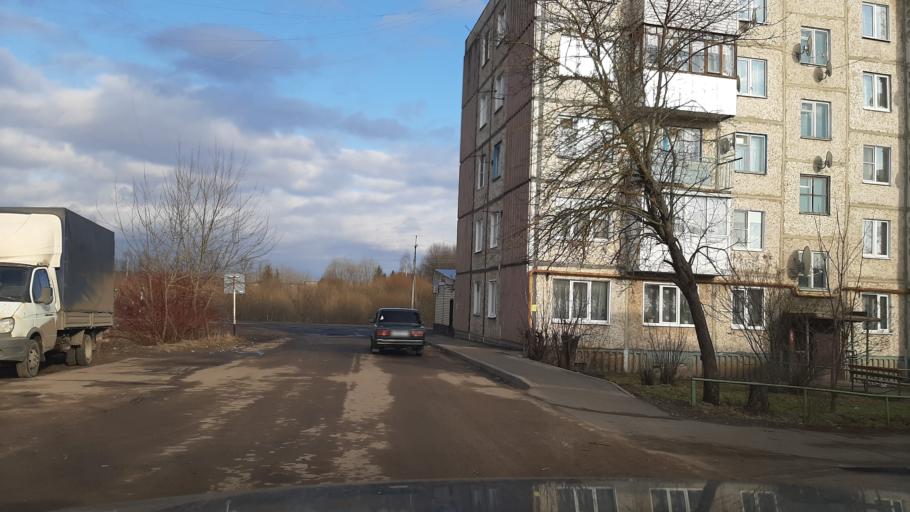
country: RU
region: Ivanovo
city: Novo-Talitsy
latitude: 56.9234
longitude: 40.7375
